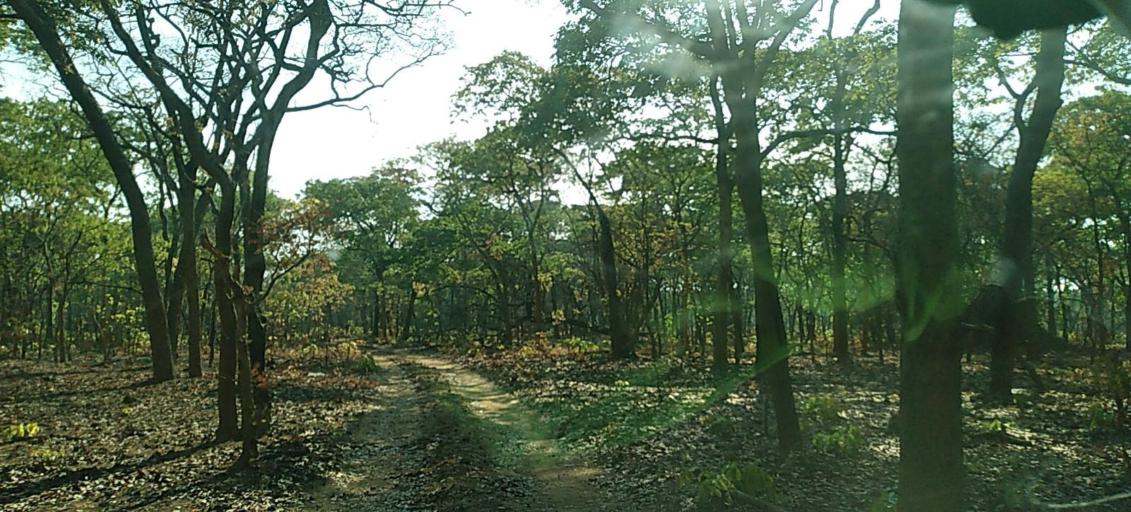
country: ZM
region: North-Western
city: Kalengwa
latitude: -13.2333
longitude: 25.0719
